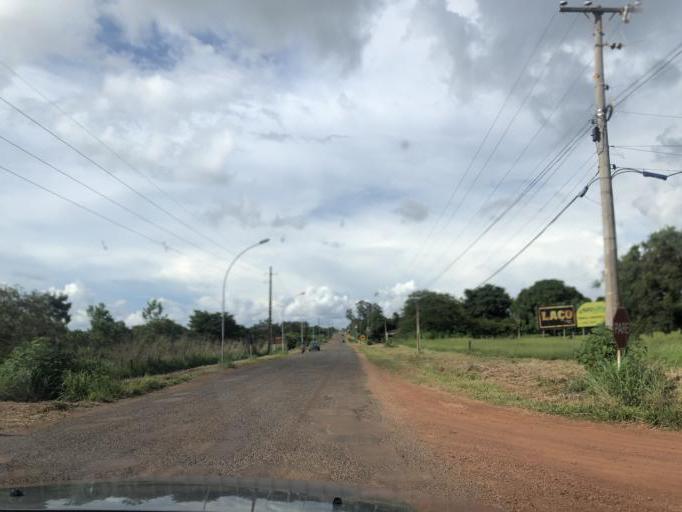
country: BR
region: Federal District
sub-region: Brasilia
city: Brasilia
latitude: -15.7448
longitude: -48.1258
